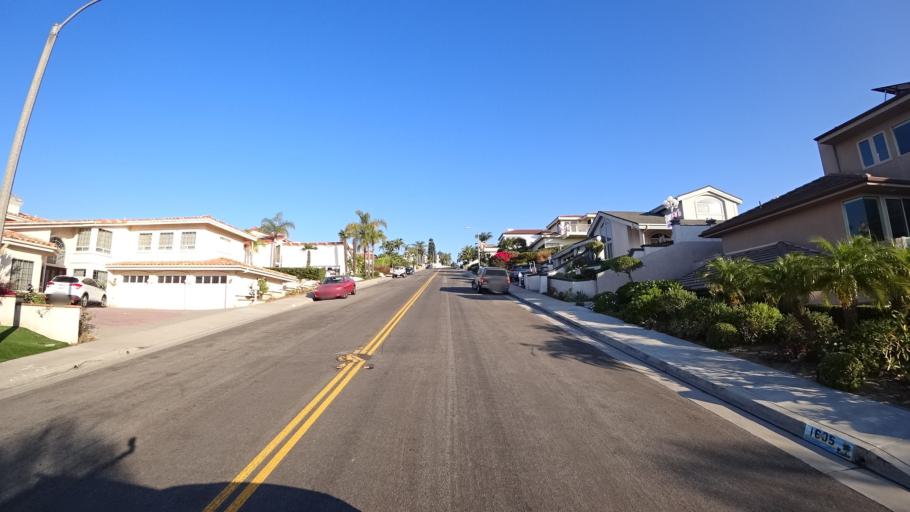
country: US
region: California
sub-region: Orange County
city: San Clemente
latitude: 33.4210
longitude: -117.5986
